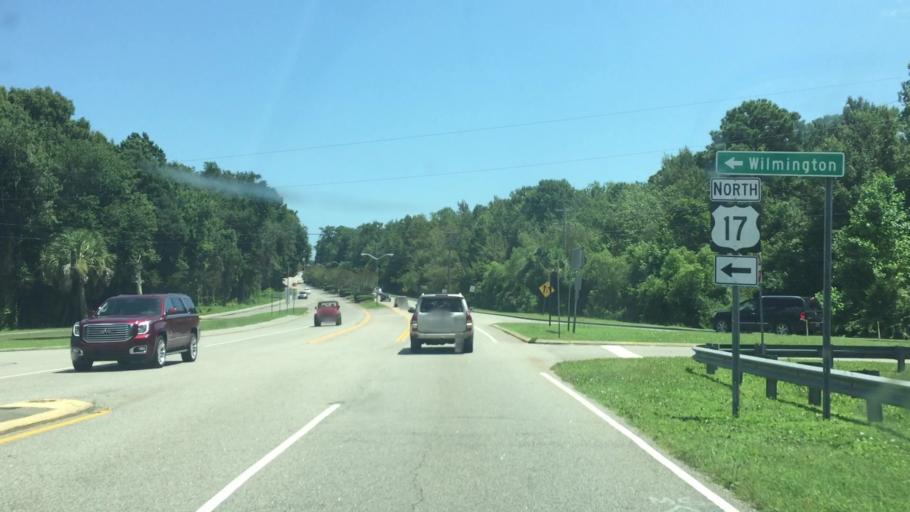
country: US
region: South Carolina
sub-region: Horry County
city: North Myrtle Beach
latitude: 33.8461
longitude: -78.6521
